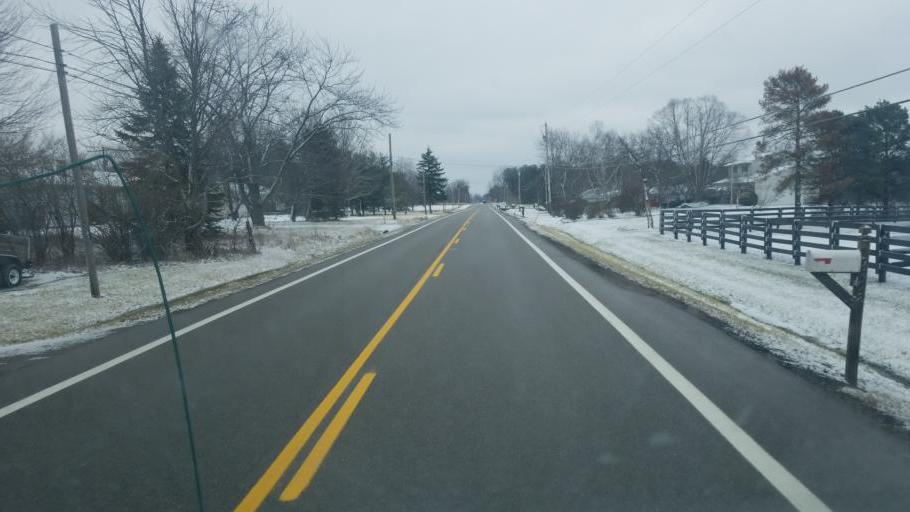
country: US
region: Ohio
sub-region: Licking County
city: Johnstown
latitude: 40.1859
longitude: -82.7526
